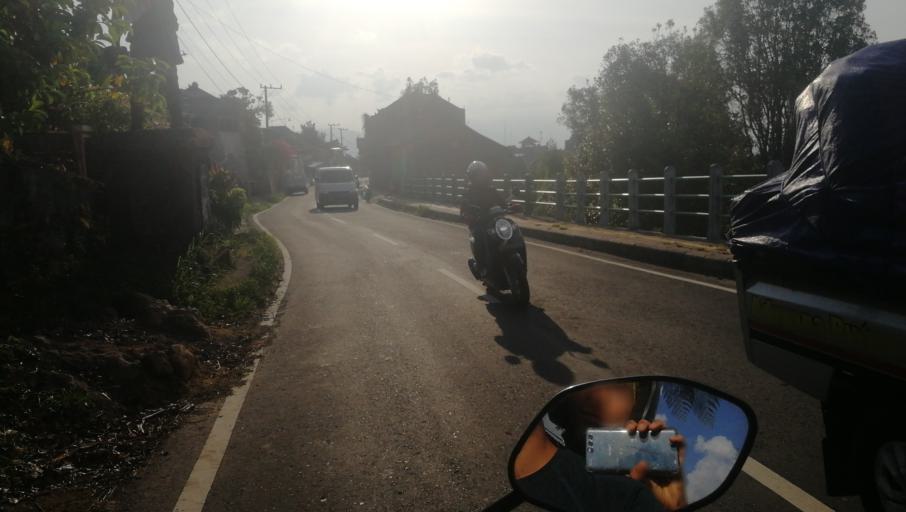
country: ID
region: Bali
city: Munduk
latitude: -8.2662
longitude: 115.0563
